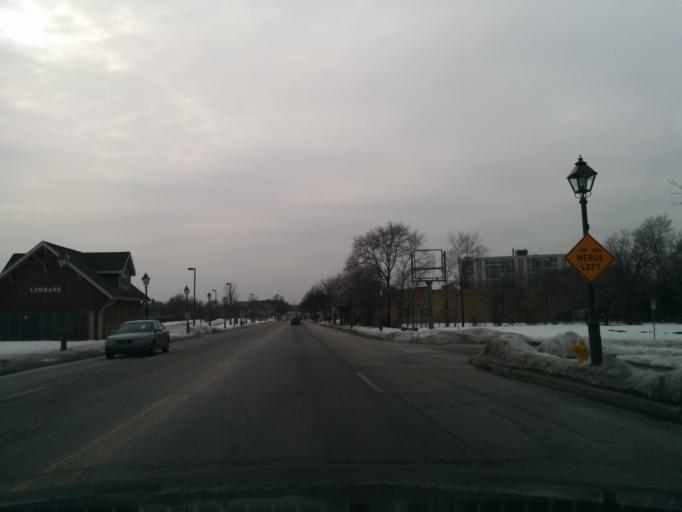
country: US
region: Illinois
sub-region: DuPage County
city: Lombard
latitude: 41.8884
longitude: -88.0134
